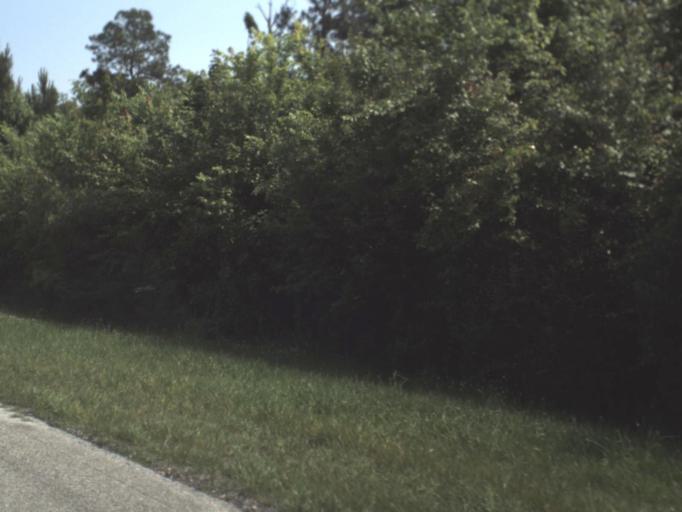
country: US
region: Florida
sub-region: Saint Johns County
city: Palm Valley
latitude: 30.0480
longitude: -81.4241
